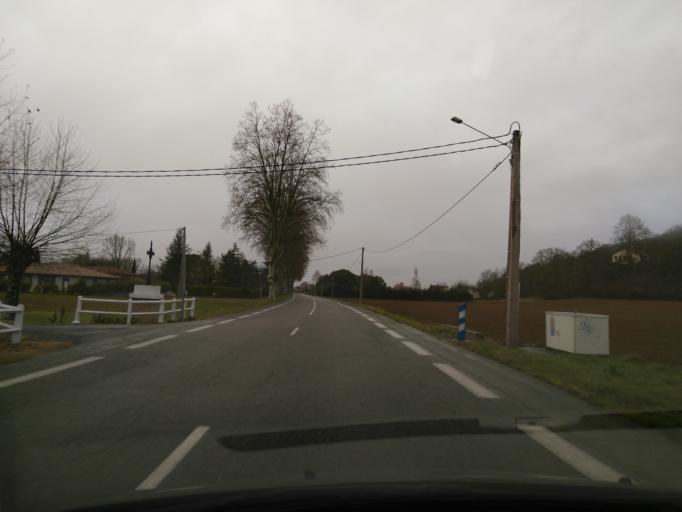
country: FR
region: Midi-Pyrenees
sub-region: Departement de la Haute-Garonne
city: Rieux-Volvestre
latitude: 43.2487
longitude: 1.2021
